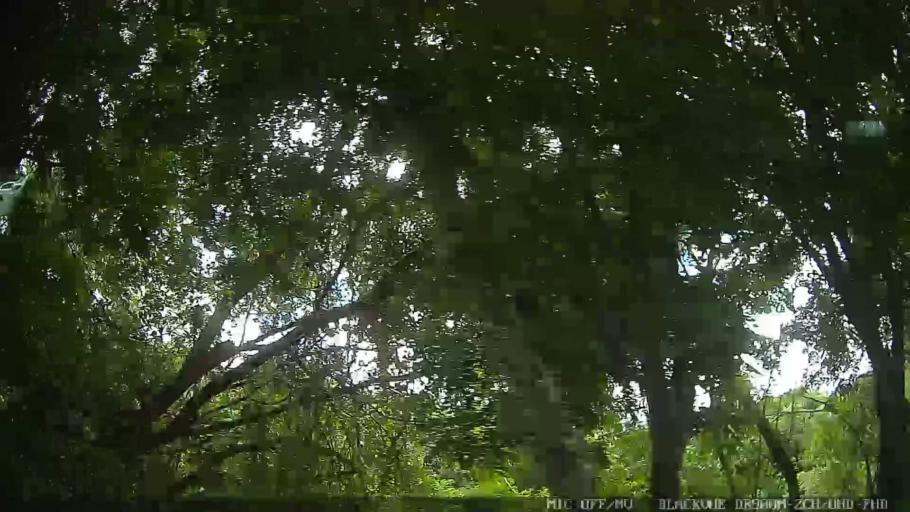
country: BR
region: Sao Paulo
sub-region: Pedreira
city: Pedreira
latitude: -22.7423
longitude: -46.9190
